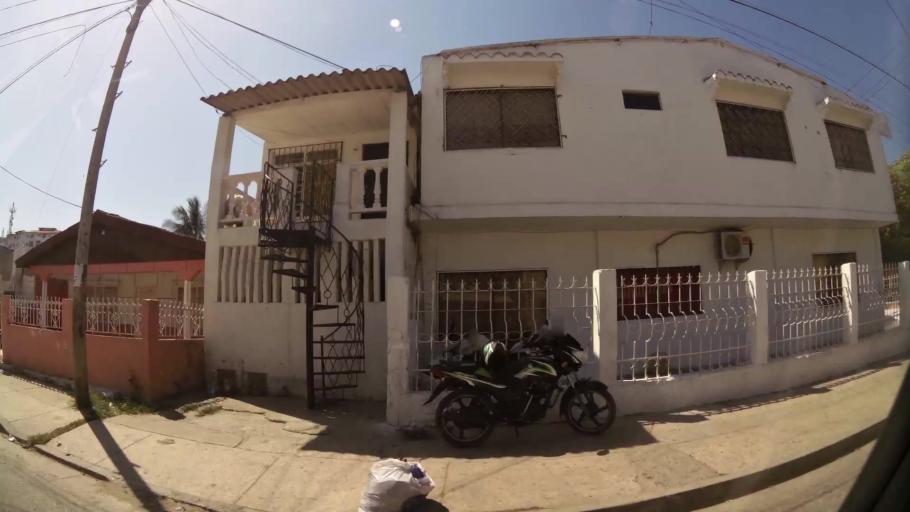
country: CO
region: Bolivar
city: Cartagena
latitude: 10.4373
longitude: -75.5210
